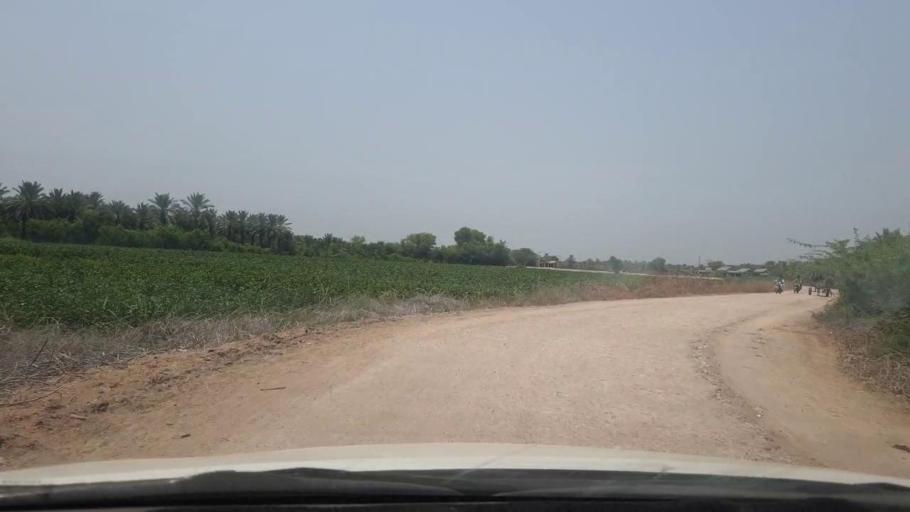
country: PK
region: Sindh
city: Khairpur
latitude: 27.5057
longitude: 68.8614
